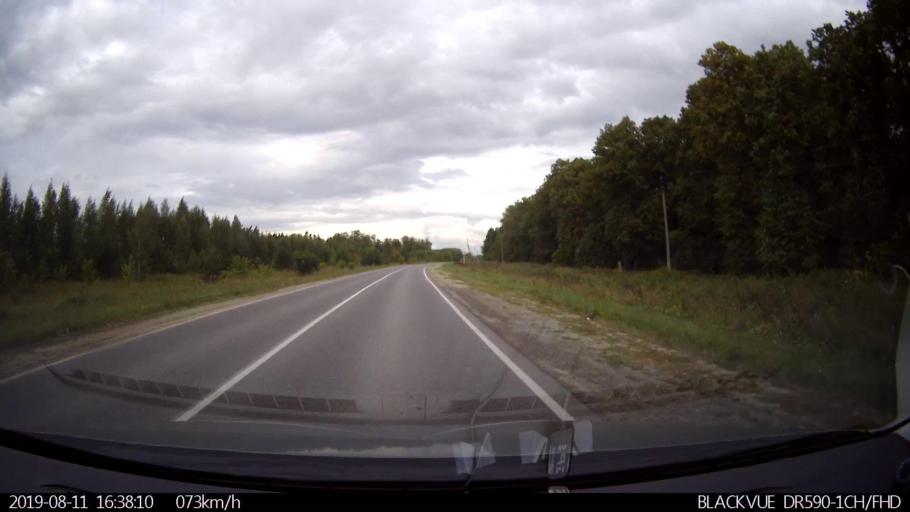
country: RU
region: Ulyanovsk
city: Mayna
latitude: 54.1332
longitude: 47.6220
